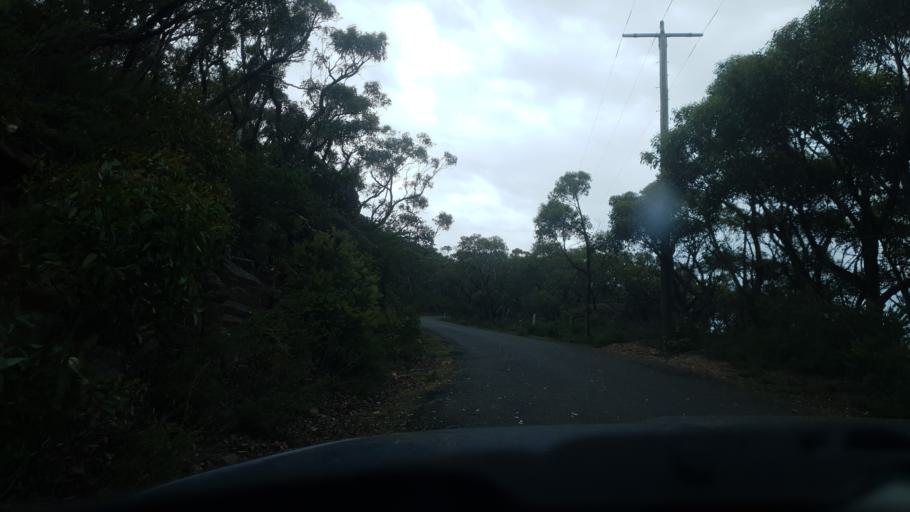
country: AU
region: Victoria
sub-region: Northern Grampians
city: Stawell
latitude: -37.2819
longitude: 142.5869
